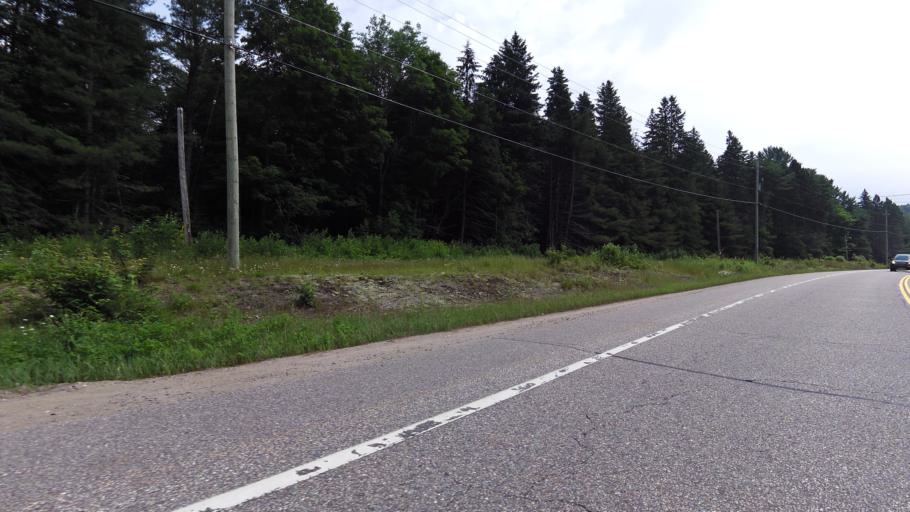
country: CA
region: Ontario
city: Mattawa
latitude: 45.5868
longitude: -78.4821
